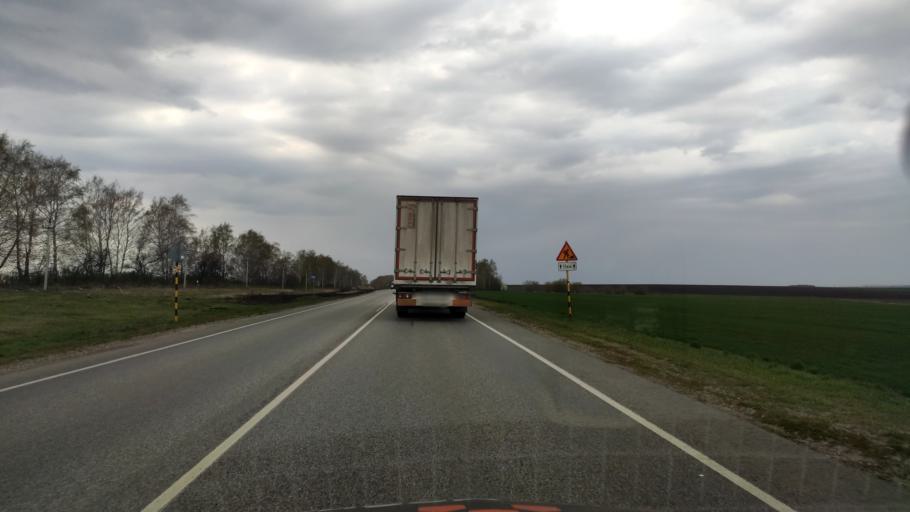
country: RU
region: Kursk
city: Gorshechnoye
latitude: 51.5486
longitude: 38.1167
